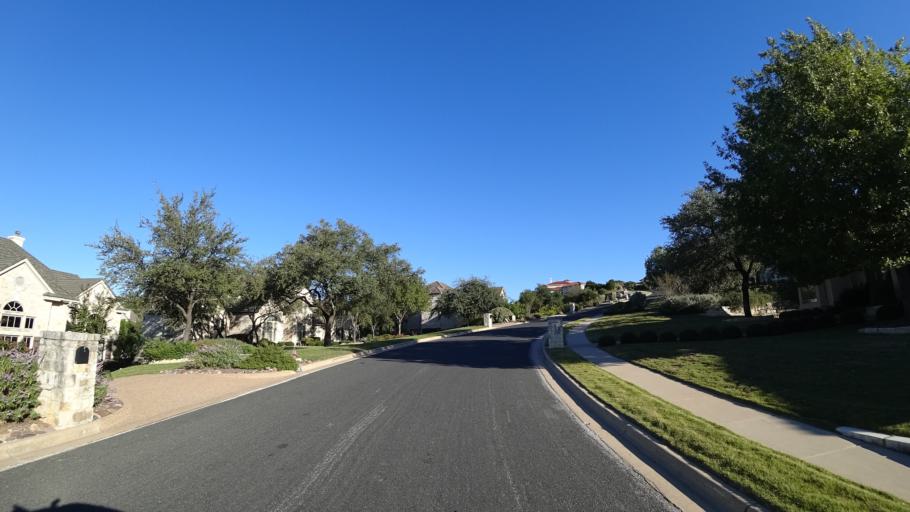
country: US
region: Texas
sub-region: Travis County
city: West Lake Hills
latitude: 30.3154
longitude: -97.8098
